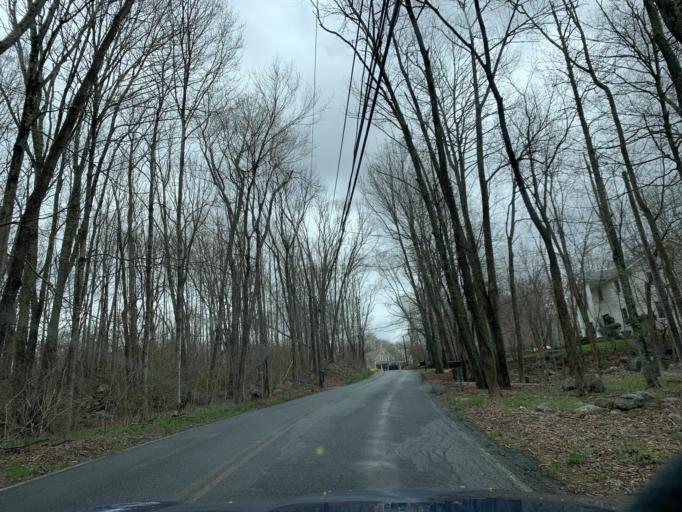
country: US
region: Massachusetts
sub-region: Bristol County
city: Rehoboth
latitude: 41.8741
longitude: -71.2067
